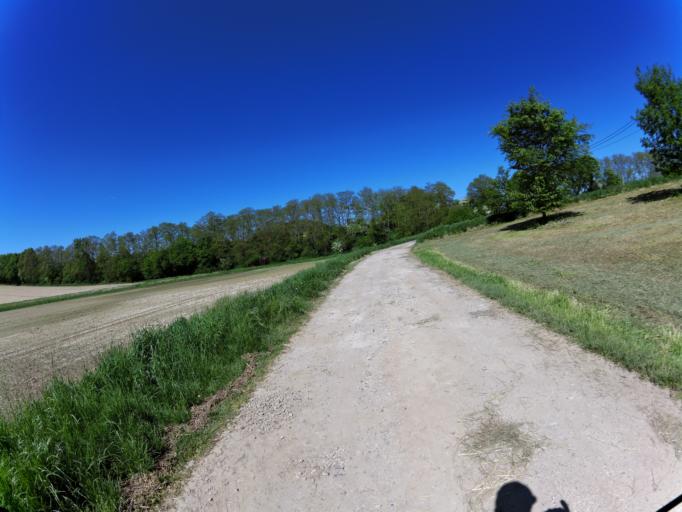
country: DE
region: North Rhine-Westphalia
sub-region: Regierungsbezirk Koln
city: Herzogenrath
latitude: 50.8876
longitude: 6.1303
